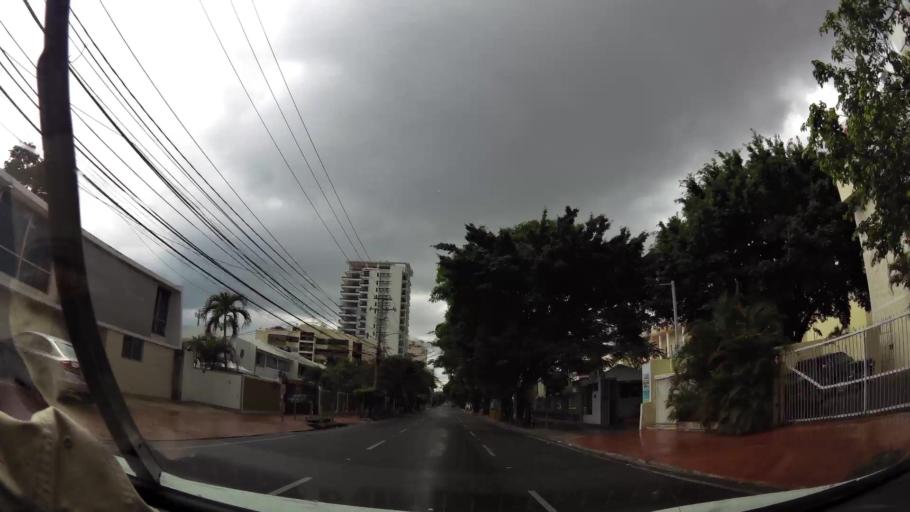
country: DO
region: Nacional
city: Ciudad Nueva
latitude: 18.4663
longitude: -69.9150
